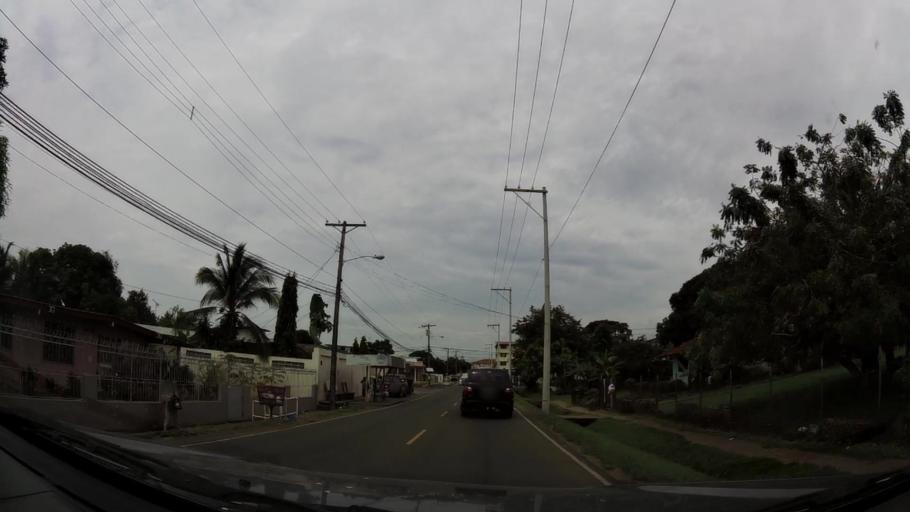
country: PA
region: Panama
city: San Miguelito
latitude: 9.0483
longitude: -79.4361
